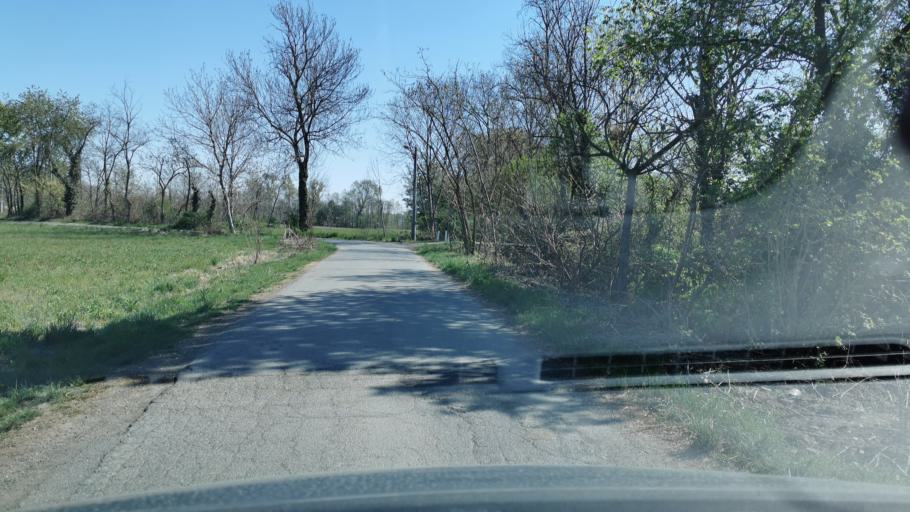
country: IT
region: Piedmont
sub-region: Provincia di Torino
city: Leini
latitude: 45.2021
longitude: 7.6973
